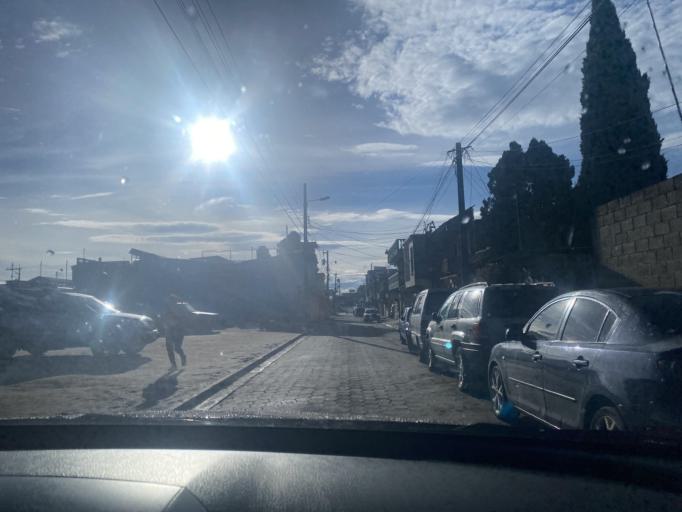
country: GT
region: Quetzaltenango
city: Olintepeque
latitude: 14.8659
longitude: -91.5208
